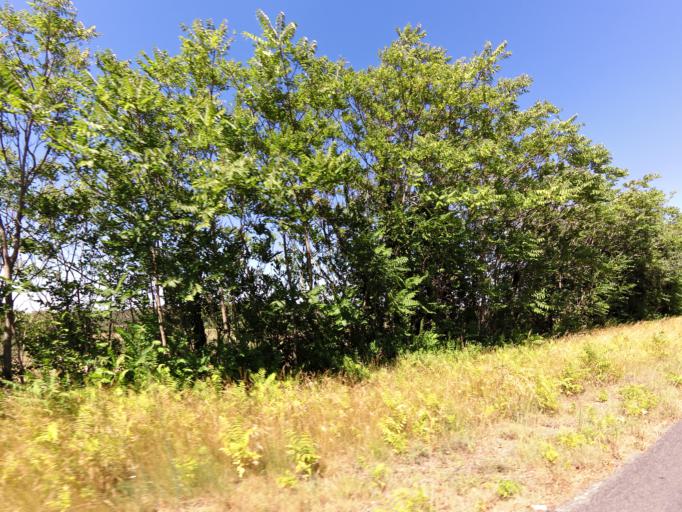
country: FR
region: Languedoc-Roussillon
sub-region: Departement du Gard
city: Aubais
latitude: 43.7495
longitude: 4.1243
